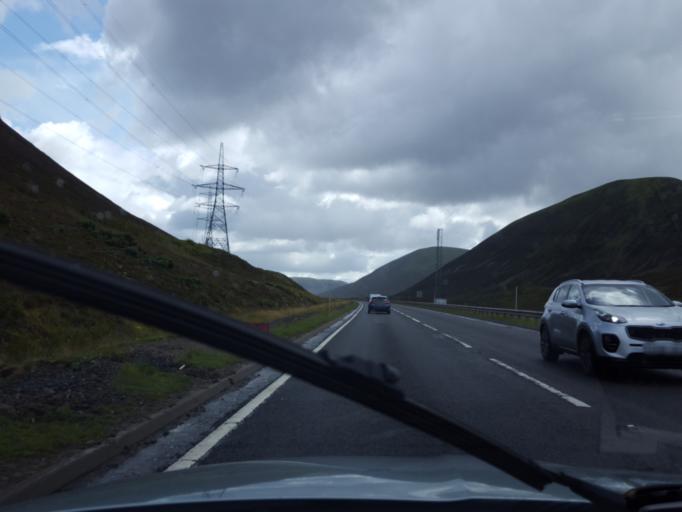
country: GB
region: Scotland
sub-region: Highland
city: Kingussie
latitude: 56.8715
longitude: -4.2567
